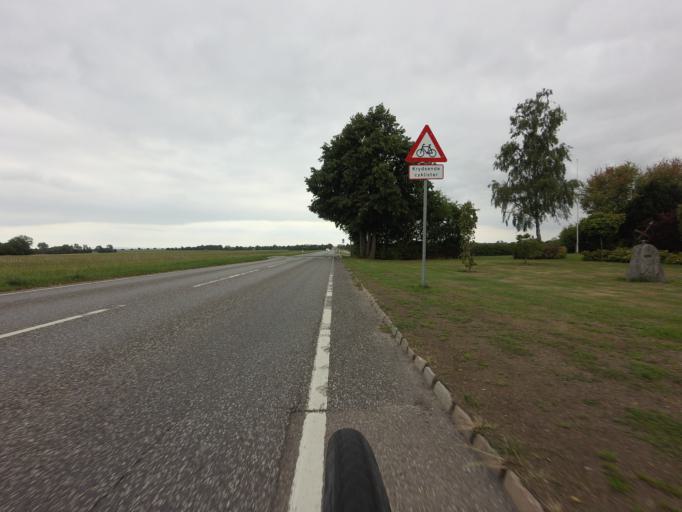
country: DK
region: Zealand
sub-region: Stevns Kommune
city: Store Heddinge
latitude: 55.2699
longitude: 12.3897
